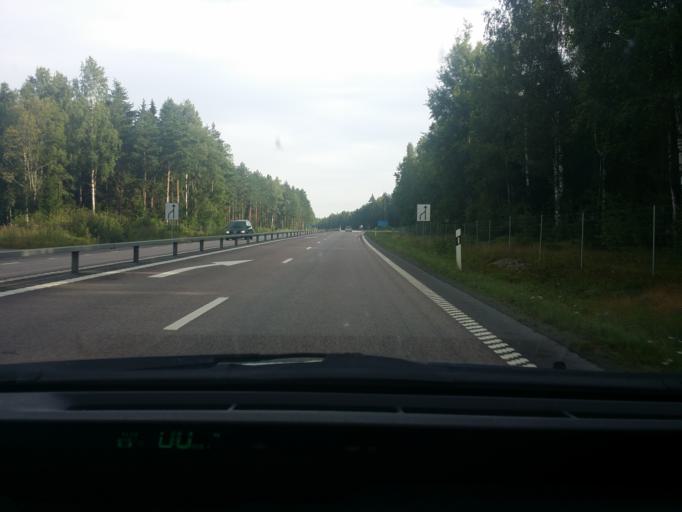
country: SE
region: Vaestmanland
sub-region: Vasteras
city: Hokasen
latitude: 59.6646
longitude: 16.5806
